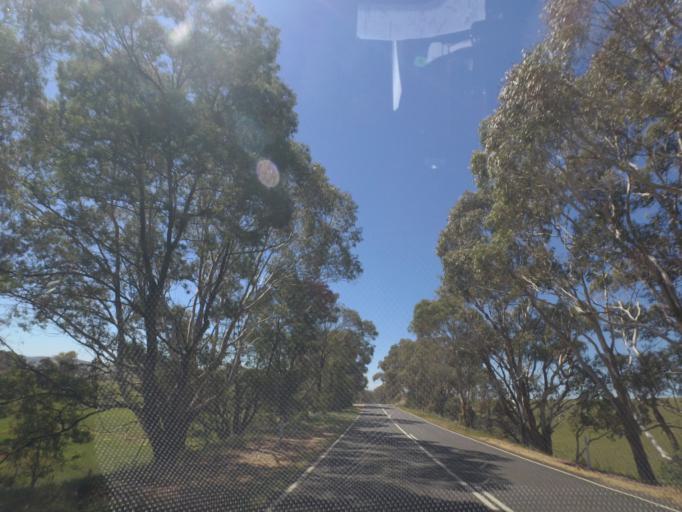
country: AU
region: Victoria
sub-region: Hume
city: Sunbury
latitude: -37.1848
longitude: 144.7418
